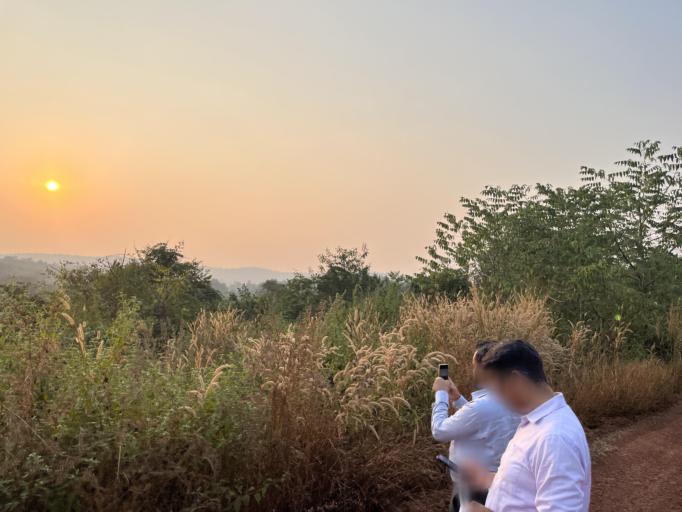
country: IN
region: Goa
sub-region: North Goa
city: Pernem
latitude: 15.7010
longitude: 73.8325
